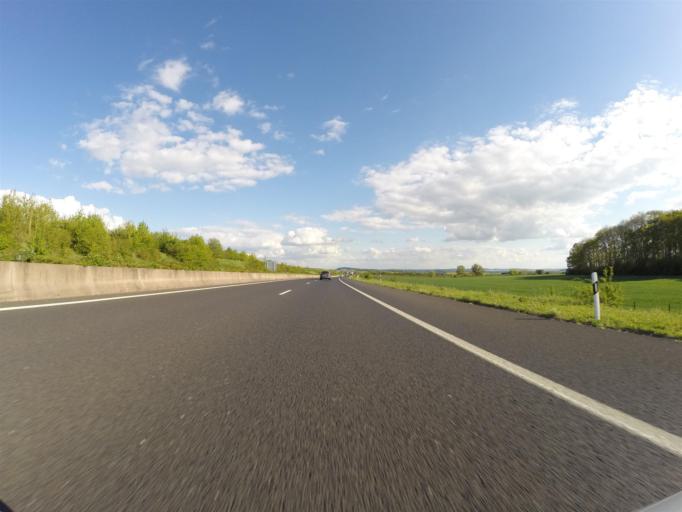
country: LU
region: Grevenmacher
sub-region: Canton de Remich
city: Mondorf-les-Bains
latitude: 49.5073
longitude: 6.3023
